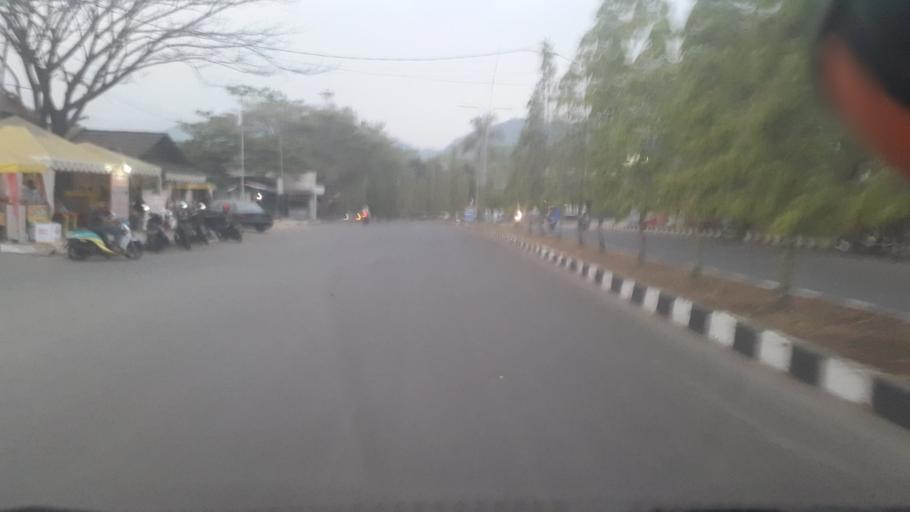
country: ID
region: West Java
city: Pelabuhanratu
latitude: -6.9961
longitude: 106.5576
